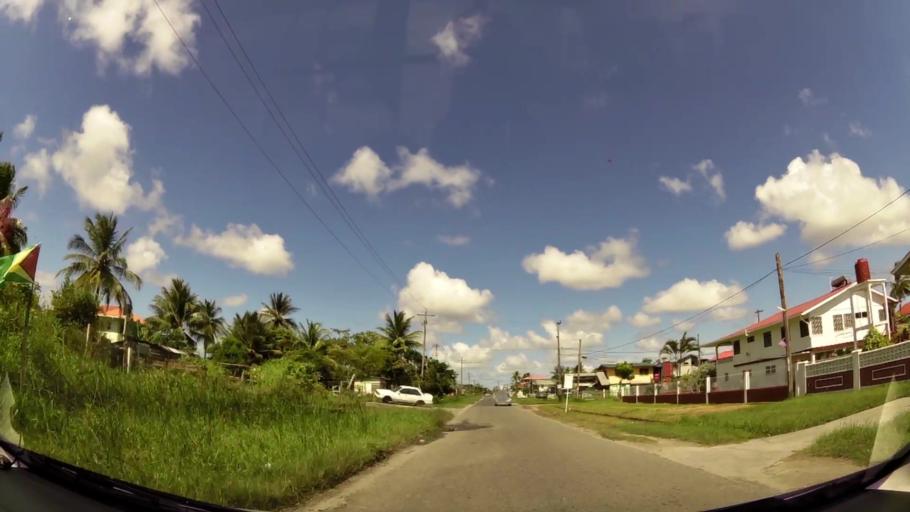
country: GY
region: Demerara-Mahaica
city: Georgetown
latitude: 6.7836
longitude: -58.1301
